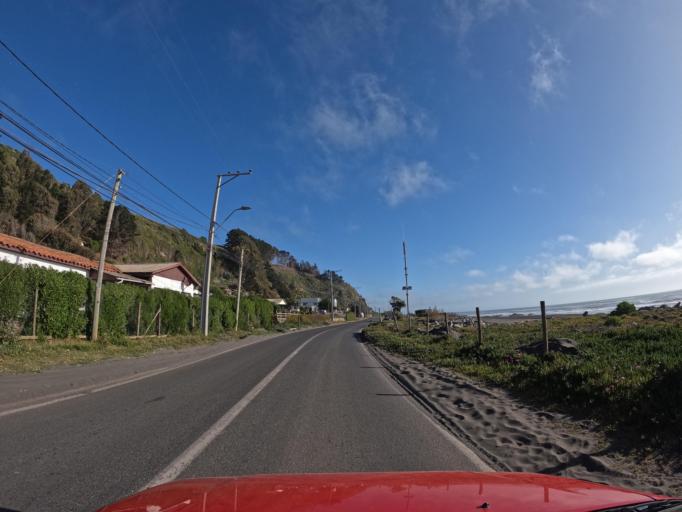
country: CL
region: Maule
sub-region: Provincia de Talca
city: Constitucion
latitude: -34.9117
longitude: -72.1815
